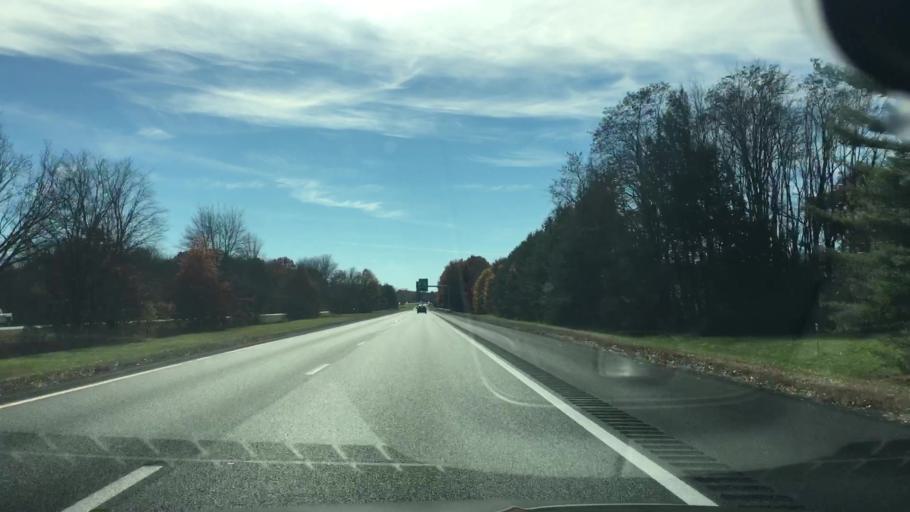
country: US
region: Massachusetts
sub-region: Hampshire County
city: Hatfield
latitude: 42.3790
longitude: -72.6322
